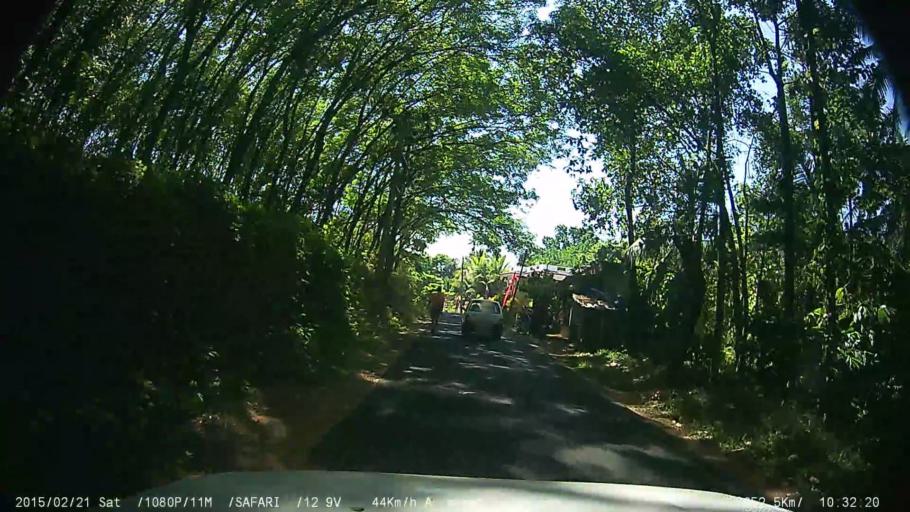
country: IN
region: Kerala
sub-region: Kottayam
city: Lalam
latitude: 9.8403
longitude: 76.7100
